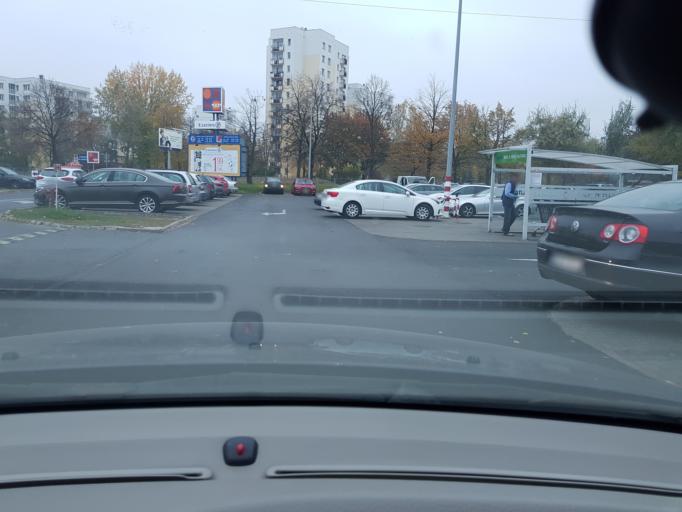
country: PL
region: Masovian Voivodeship
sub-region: Warszawa
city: Ursynow
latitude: 52.1543
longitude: 21.0415
